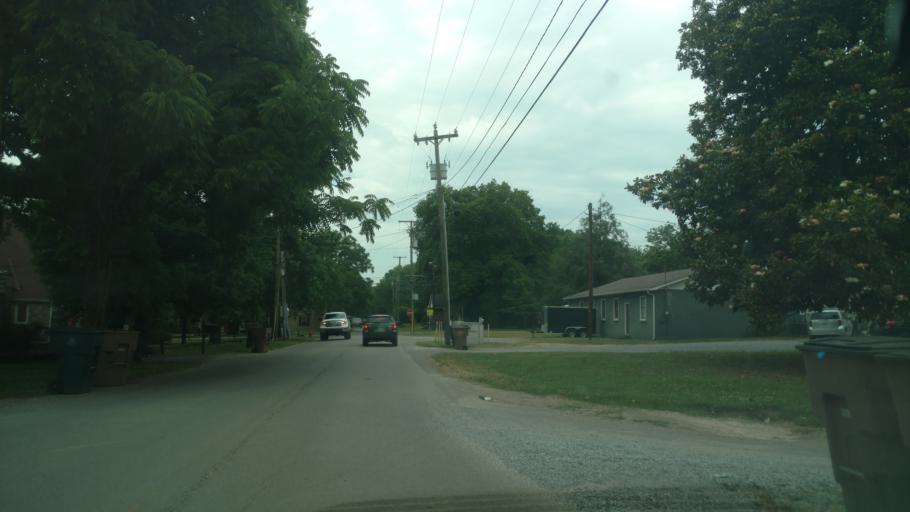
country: US
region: Tennessee
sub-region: Davidson County
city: Nashville
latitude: 36.1891
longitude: -86.7254
